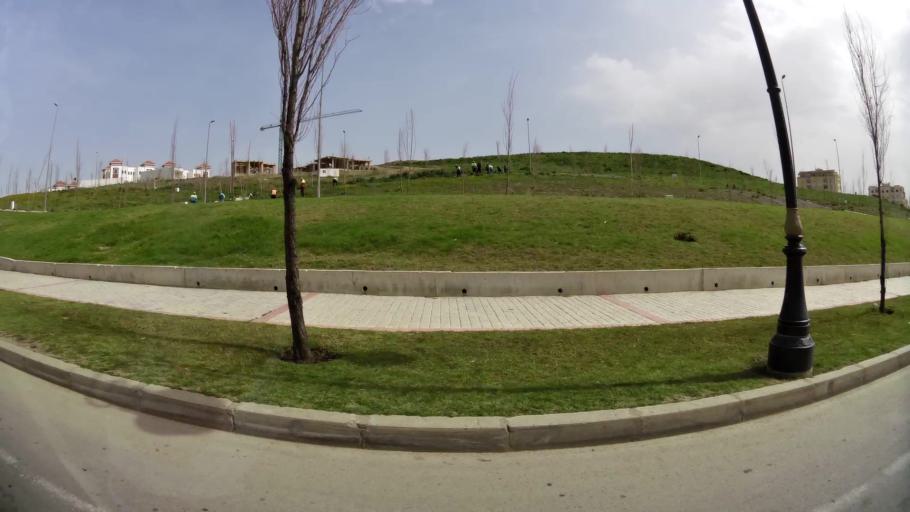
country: MA
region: Tanger-Tetouan
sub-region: Tanger-Assilah
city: Boukhalef
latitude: 35.7431
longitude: -5.8657
